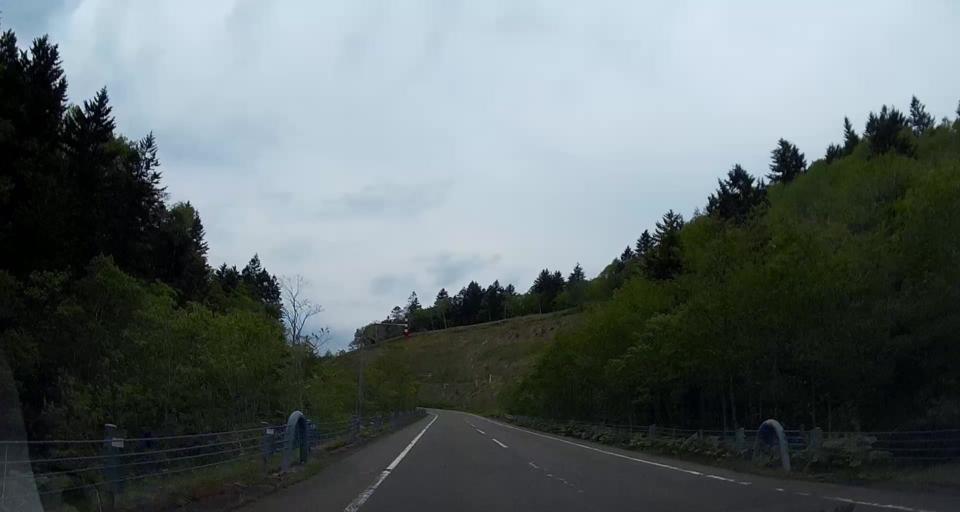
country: JP
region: Hokkaido
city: Shiraoi
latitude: 42.6777
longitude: 141.1324
